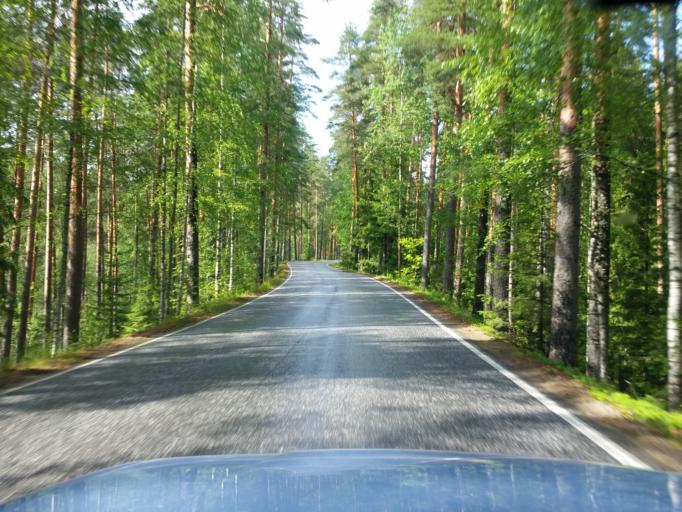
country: FI
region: Southern Savonia
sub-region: Savonlinna
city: Sulkava
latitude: 61.7894
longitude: 28.4249
